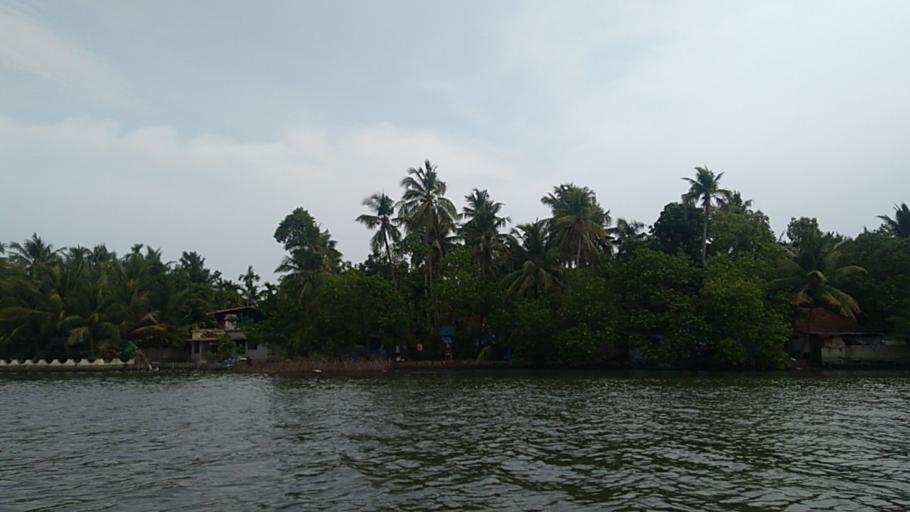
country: IN
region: Kerala
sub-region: Ernakulam
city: Elur
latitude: 10.0730
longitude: 76.2430
